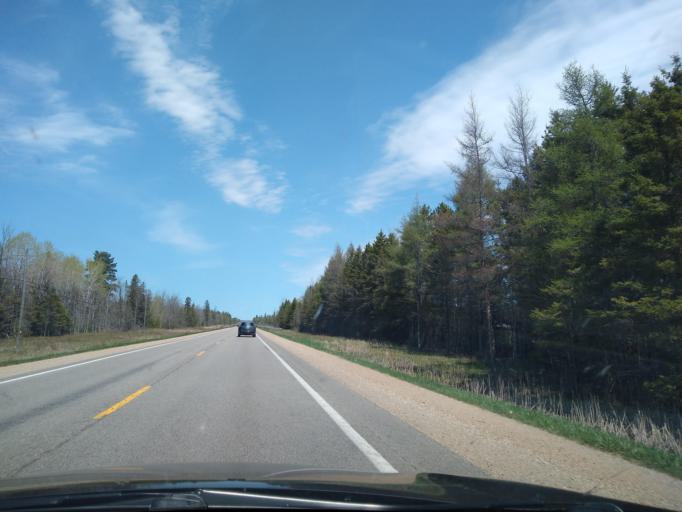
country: US
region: Michigan
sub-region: Delta County
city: Gladstone
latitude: 45.9483
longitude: -86.9720
